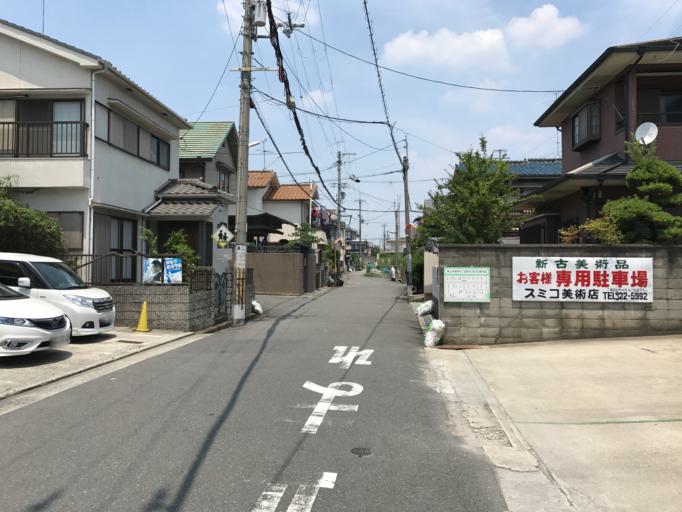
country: JP
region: Osaka
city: Yao
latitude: 34.6261
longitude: 135.6284
